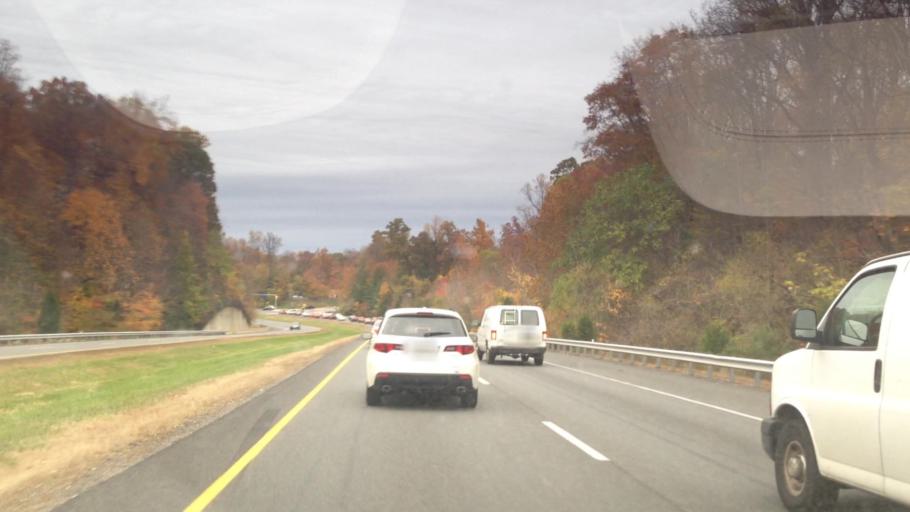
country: US
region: Virginia
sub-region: Fairfax County
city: Fairfax Station
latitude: 38.7935
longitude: -77.3344
